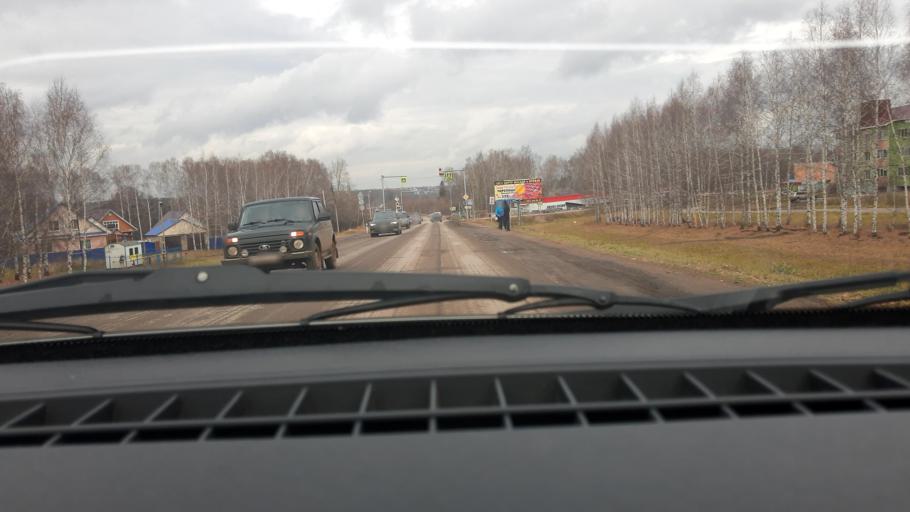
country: RU
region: Bashkortostan
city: Iglino
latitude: 54.8278
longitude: 56.4242
